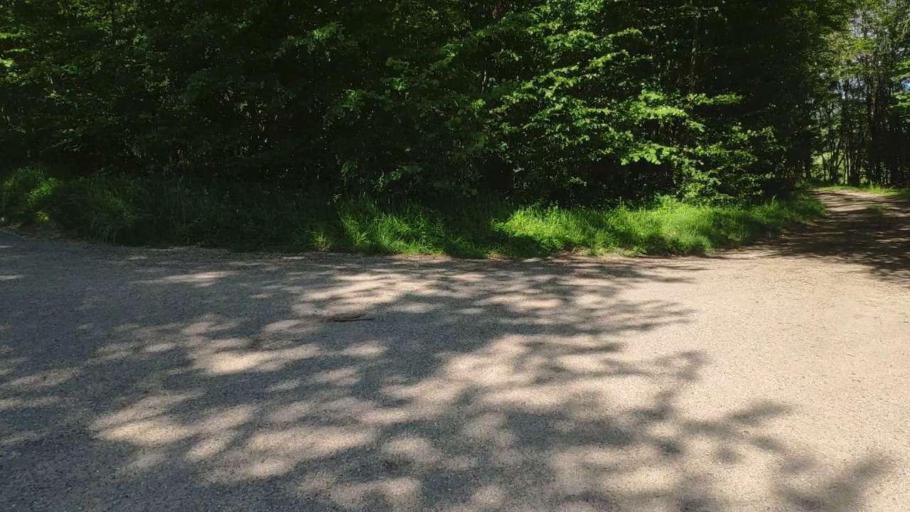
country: FR
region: Franche-Comte
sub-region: Departement du Jura
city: Bletterans
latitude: 46.7712
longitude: 5.4773
